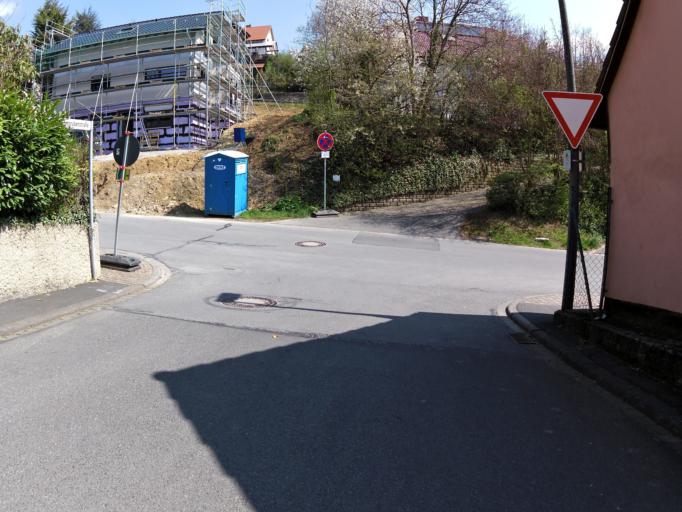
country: DE
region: Bavaria
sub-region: Regierungsbezirk Unterfranken
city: Theilheim
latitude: 49.7559
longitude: 10.0346
